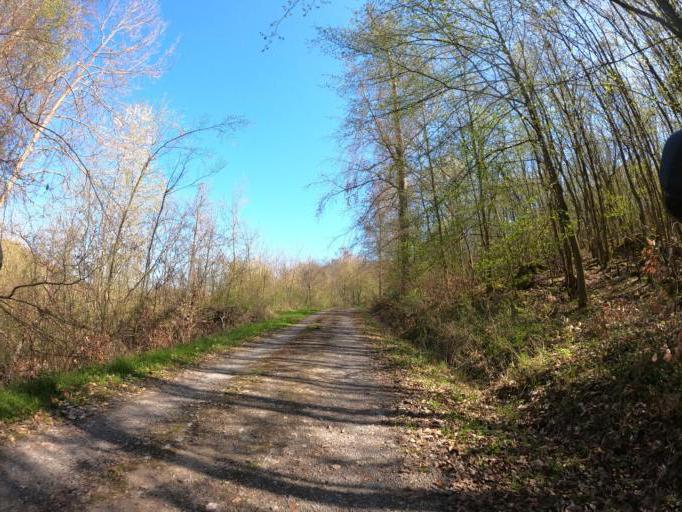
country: DE
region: Baden-Wuerttemberg
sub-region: Karlsruhe Region
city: Illingen
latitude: 48.9076
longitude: 8.9052
